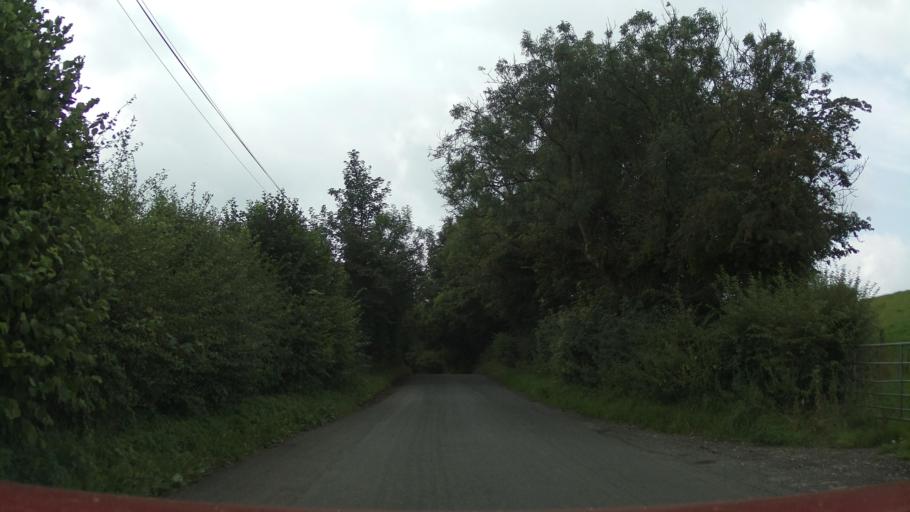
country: GB
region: England
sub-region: Somerset
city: Evercreech
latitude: 51.1750
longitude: -2.5074
